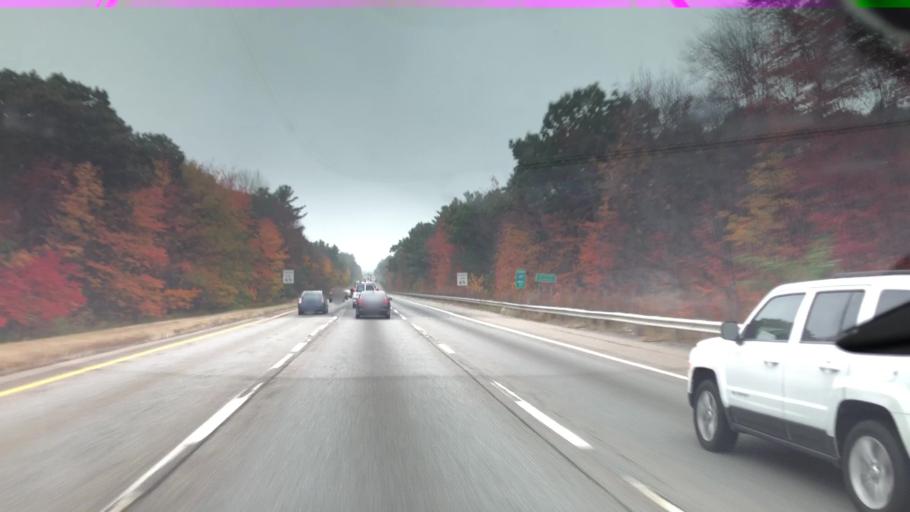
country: US
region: Massachusetts
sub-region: Middlesex County
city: Littleton Common
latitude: 42.5141
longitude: -71.5161
